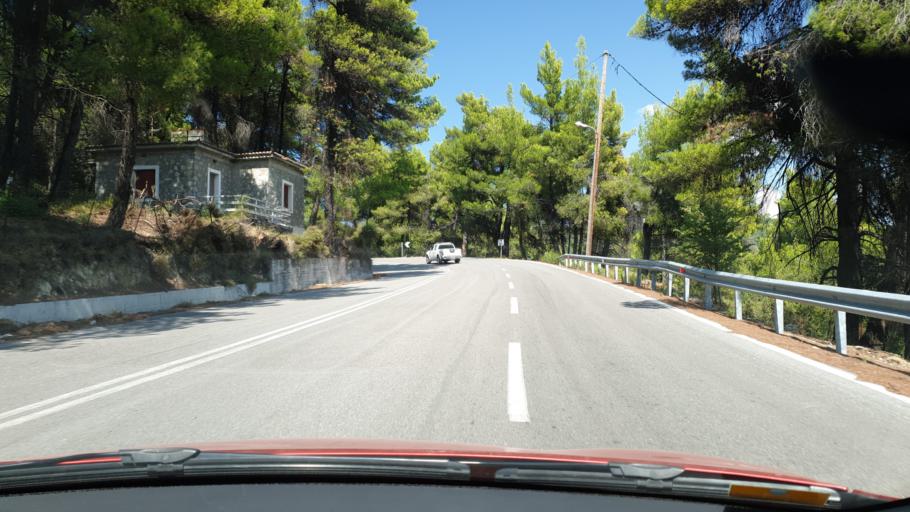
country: GR
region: Central Greece
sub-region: Nomos Evvoias
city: Politika
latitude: 38.6420
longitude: 23.5649
